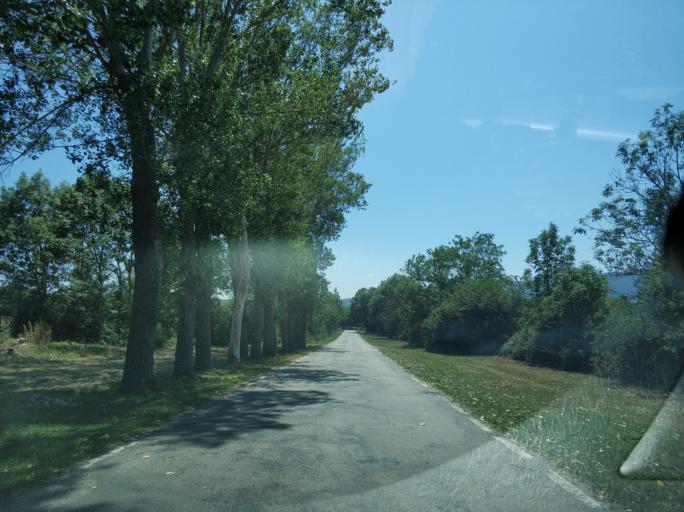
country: ES
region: Cantabria
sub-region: Provincia de Cantabria
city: Reinosa
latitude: 43.0185
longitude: -4.1637
